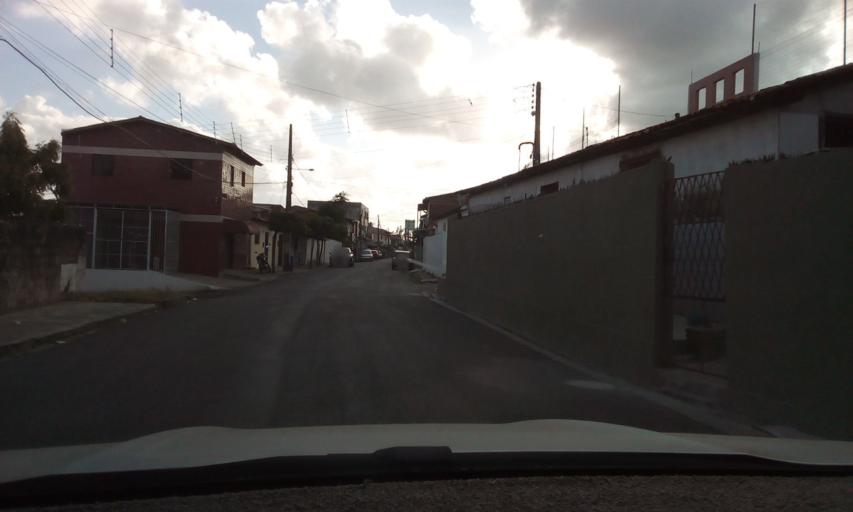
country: BR
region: Paraiba
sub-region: Joao Pessoa
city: Joao Pessoa
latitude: -7.0966
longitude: -34.8625
